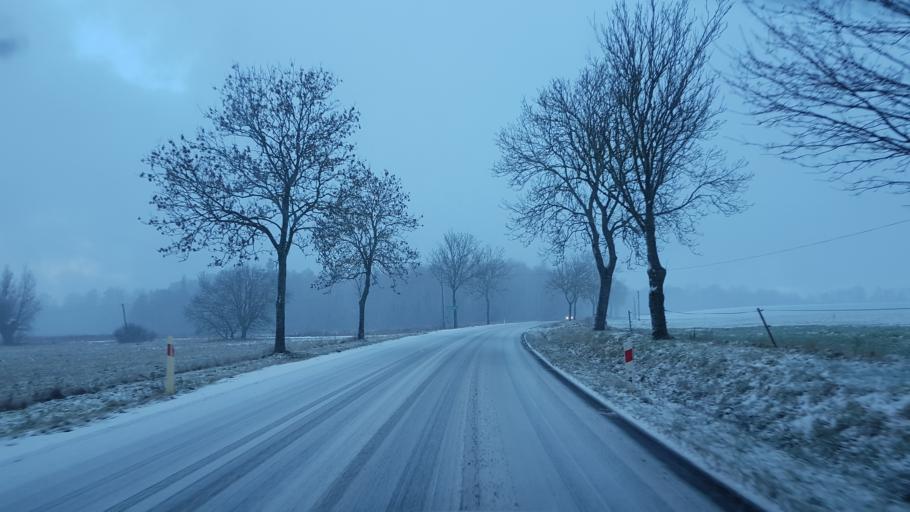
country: PL
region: West Pomeranian Voivodeship
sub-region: Powiat gryficki
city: Cerkwica
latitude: 53.9918
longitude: 15.1263
